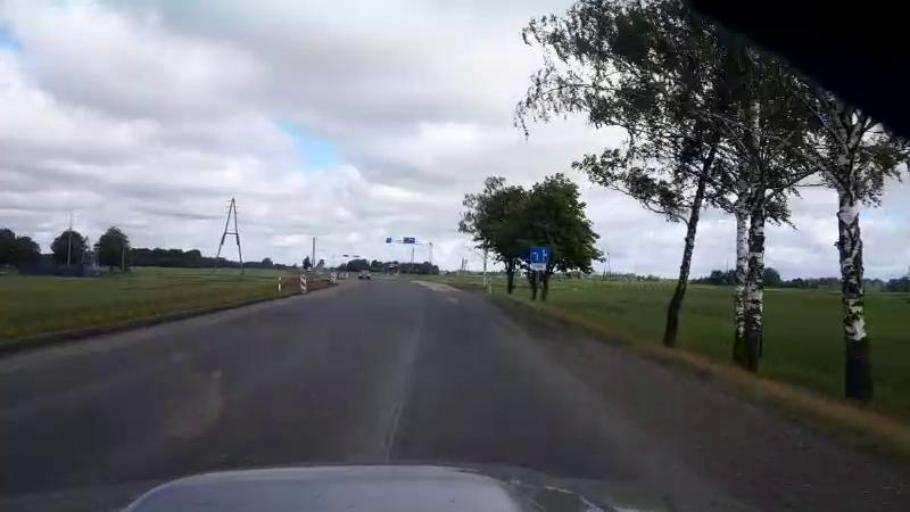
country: LV
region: Bauskas Rajons
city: Bauska
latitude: 56.2905
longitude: 24.3539
